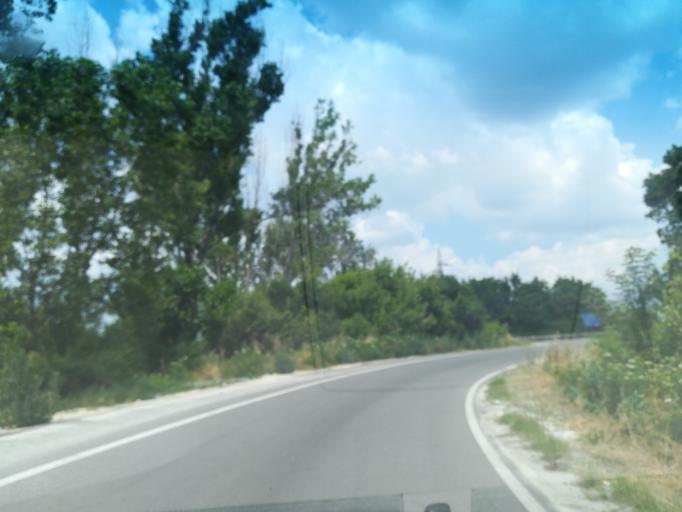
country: BG
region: Plovdiv
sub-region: Obshtina Plovdiv
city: Plovdiv
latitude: 42.2027
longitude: 24.6667
